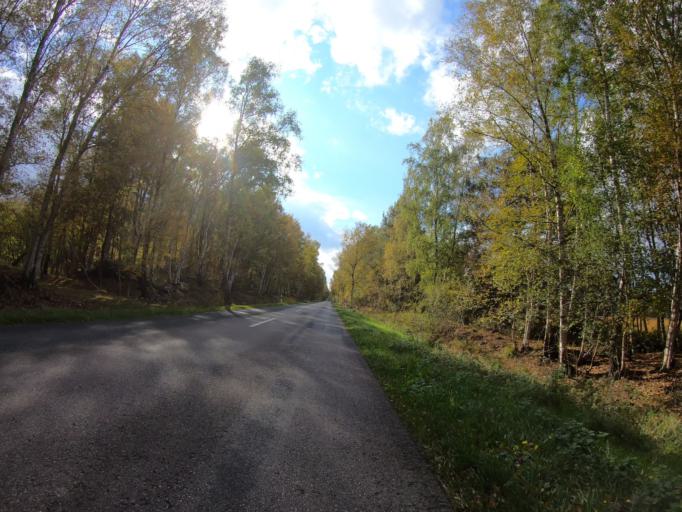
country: DE
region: Lower Saxony
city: Sassenburg
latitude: 52.5707
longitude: 10.6327
